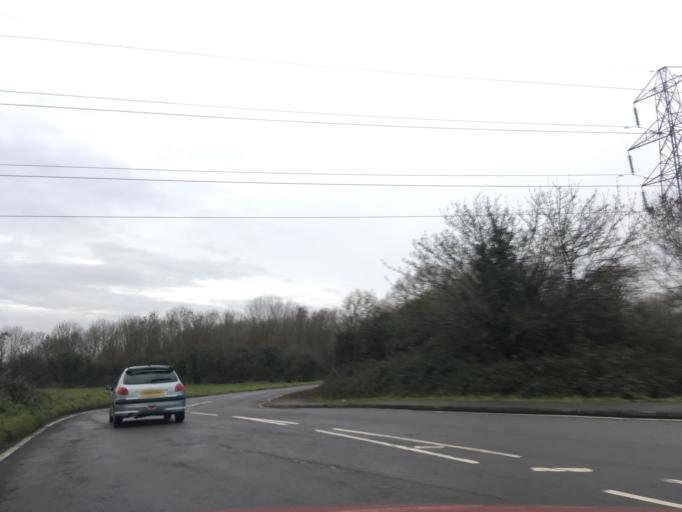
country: GB
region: Wales
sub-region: Newport
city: Nash
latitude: 51.5629
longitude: -2.9472
